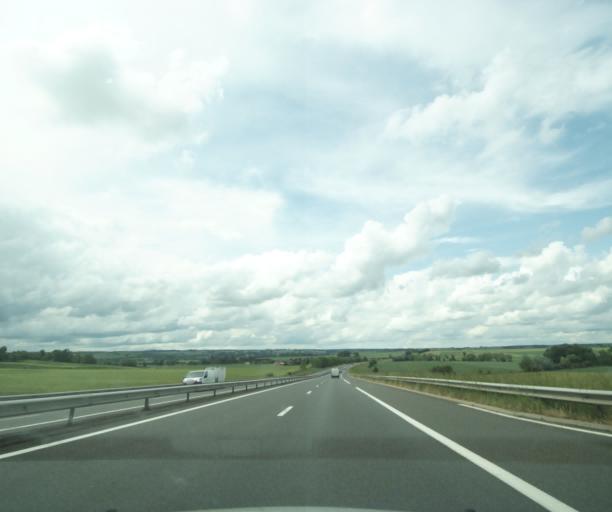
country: FR
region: Auvergne
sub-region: Departement de l'Allier
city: Bellenaves
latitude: 46.1818
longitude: 3.1190
